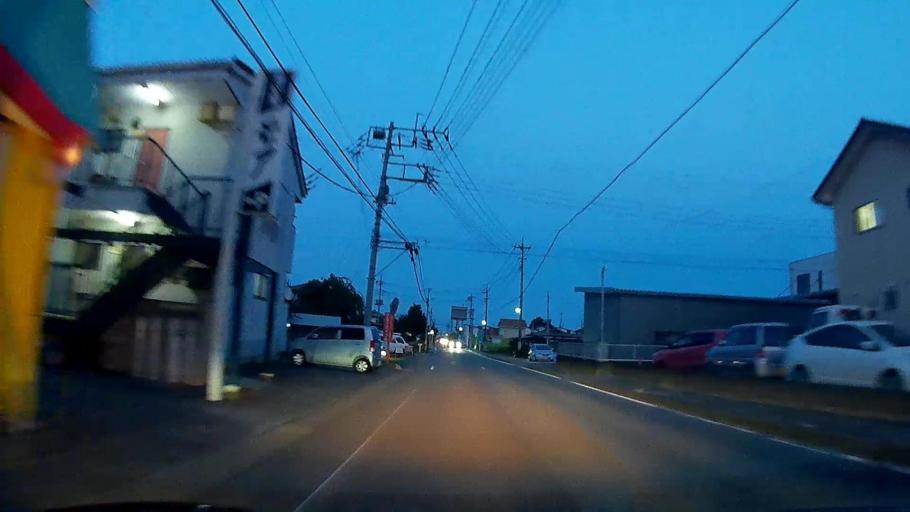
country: JP
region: Gunma
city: Takasaki
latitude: 36.3424
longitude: 138.9680
